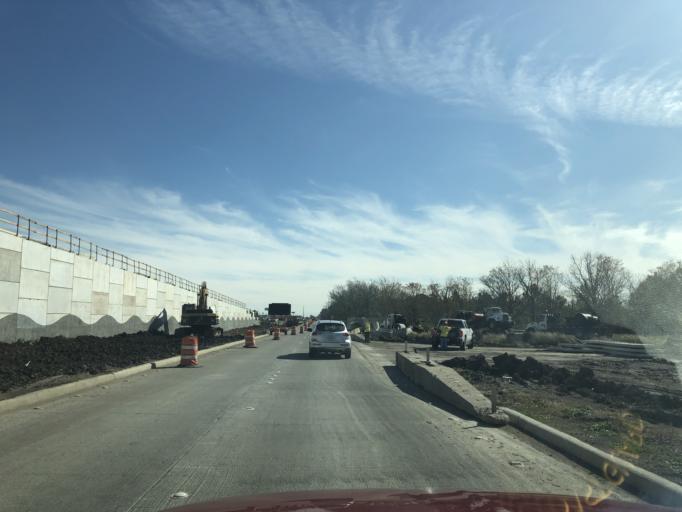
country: US
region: Texas
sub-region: Galveston County
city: Dickinson
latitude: 29.4650
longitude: -95.0904
